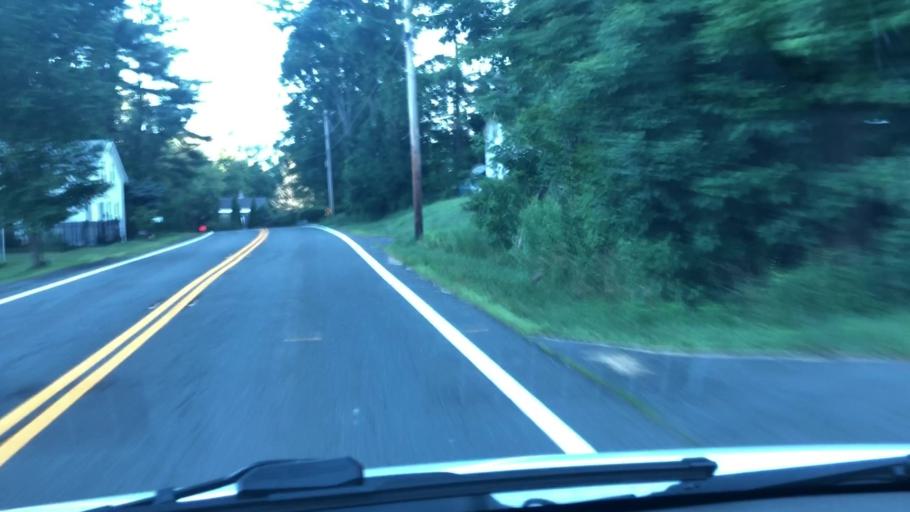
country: US
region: Massachusetts
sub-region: Hampshire County
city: Chesterfield
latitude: 42.3685
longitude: -72.9098
